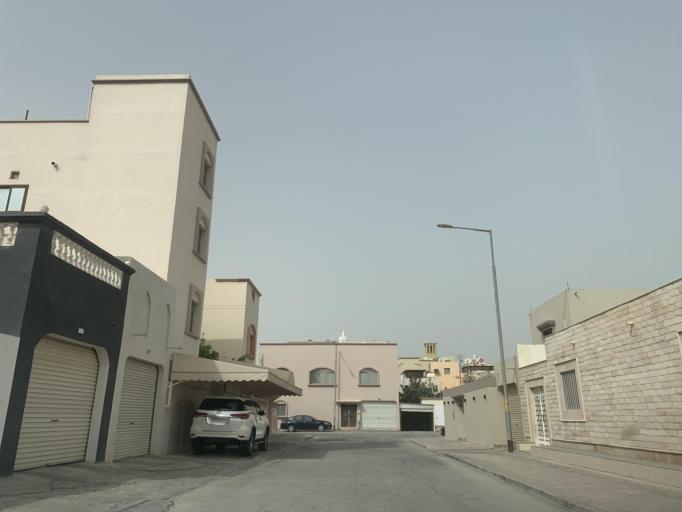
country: BH
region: Northern
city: Madinat `Isa
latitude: 26.1614
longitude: 50.5712
